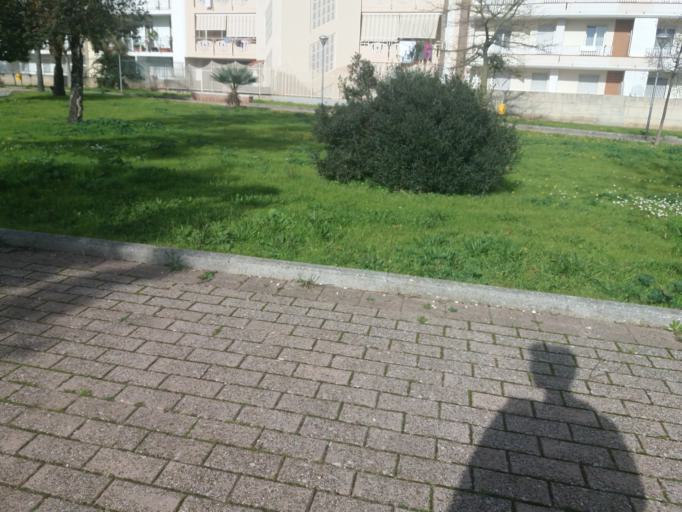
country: IT
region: Apulia
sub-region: Provincia di Barletta - Andria - Trani
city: Andria
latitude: 41.2354
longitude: 16.3005
